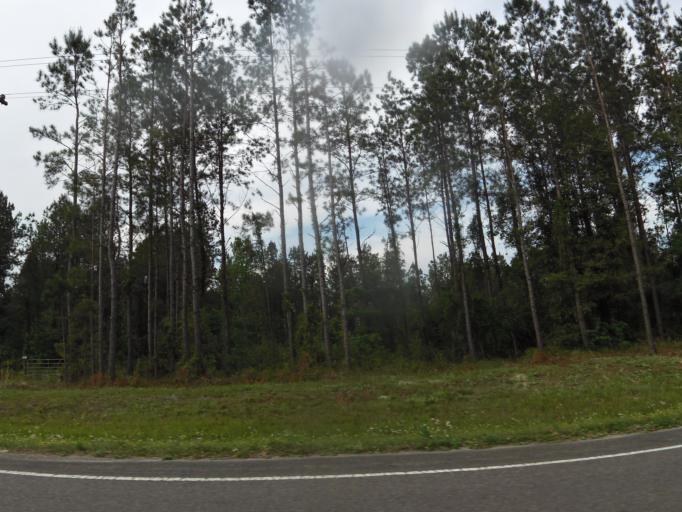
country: US
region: Florida
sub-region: Nassau County
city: Hilliard
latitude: 30.6947
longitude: -81.8481
